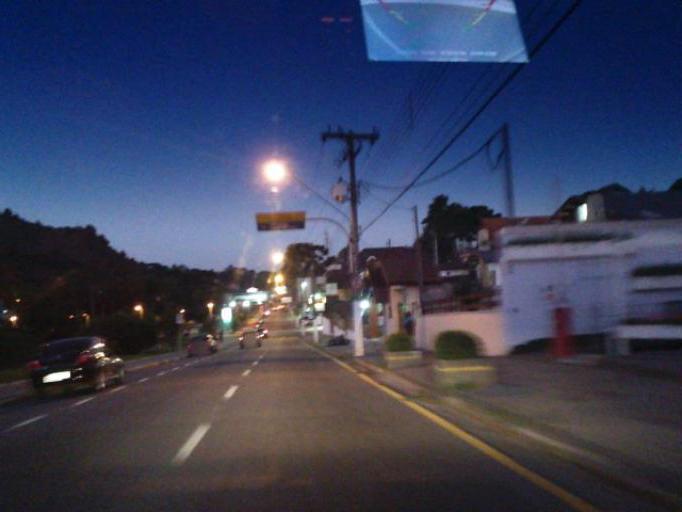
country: BR
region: Sao Paulo
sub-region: Campos Do Jordao
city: Campos do Jordao
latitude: -22.7198
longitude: -45.5706
